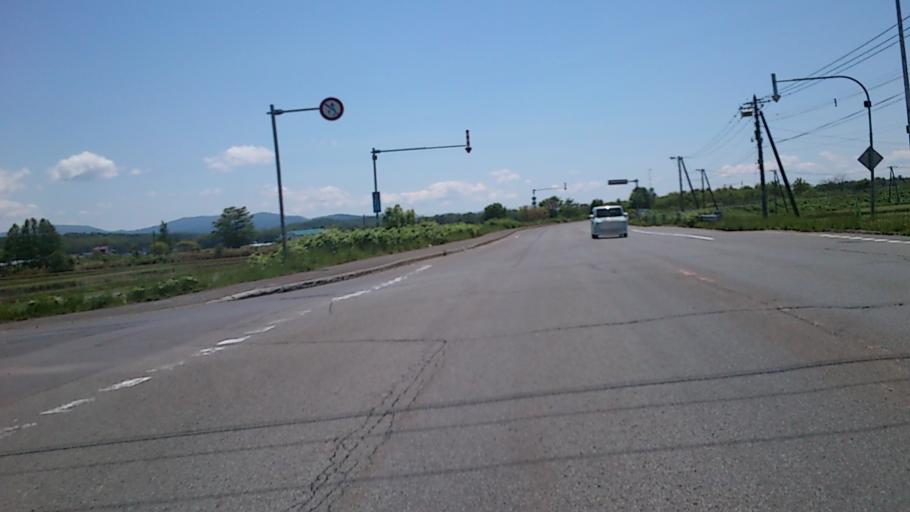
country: JP
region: Hokkaido
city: Nayoro
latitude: 44.3169
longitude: 142.4570
